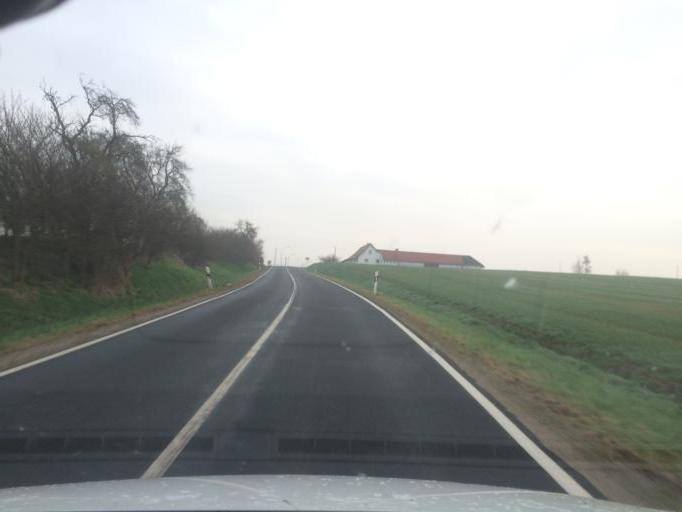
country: DE
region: Lower Saxony
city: Bad Sachsa
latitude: 51.5374
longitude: 10.5217
